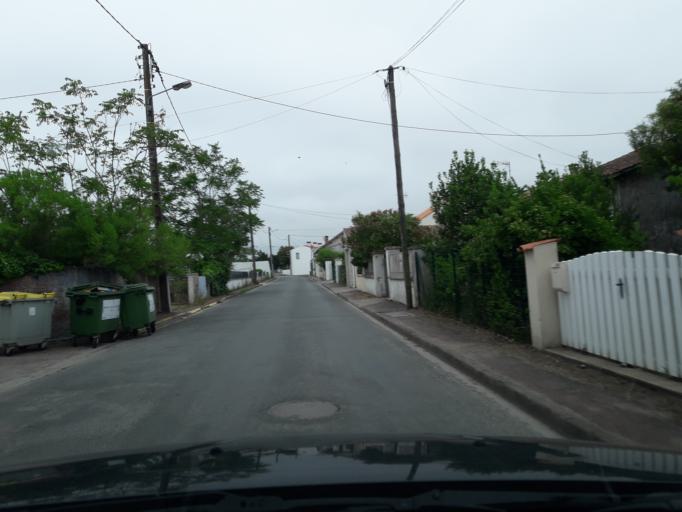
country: FR
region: Poitou-Charentes
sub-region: Departement de la Charente-Maritime
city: Boyard-Ville
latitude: 45.9663
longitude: -1.2436
